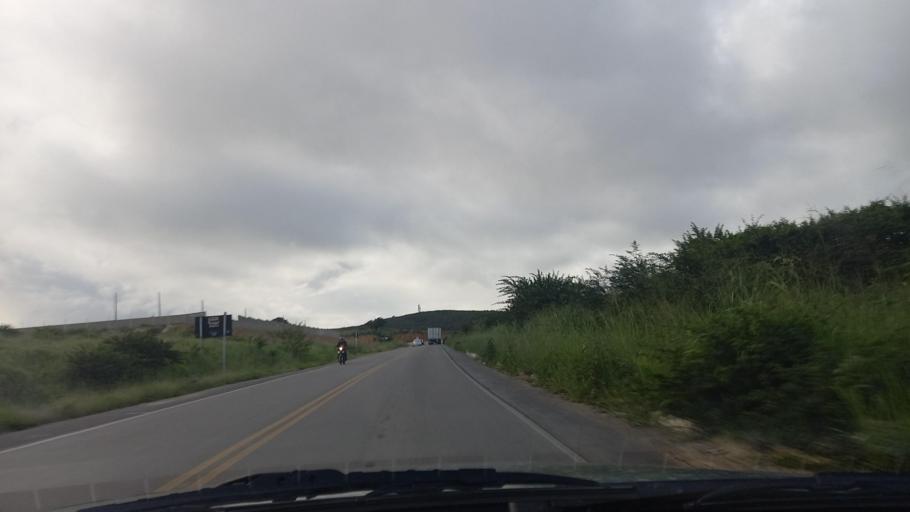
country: BR
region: Pernambuco
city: Garanhuns
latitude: -8.8908
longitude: -36.5062
